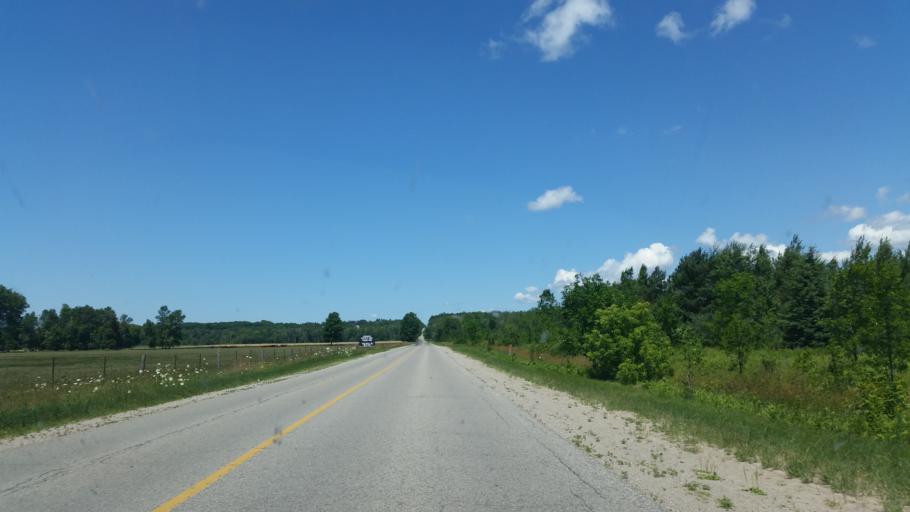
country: CA
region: Ontario
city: Barrie
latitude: 44.4557
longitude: -79.7900
